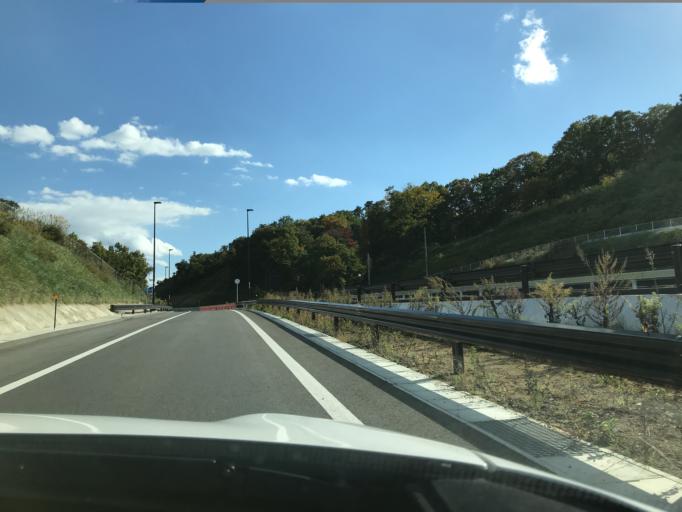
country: JP
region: Fukushima
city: Hobaramachi
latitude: 37.7633
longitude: 140.5923
